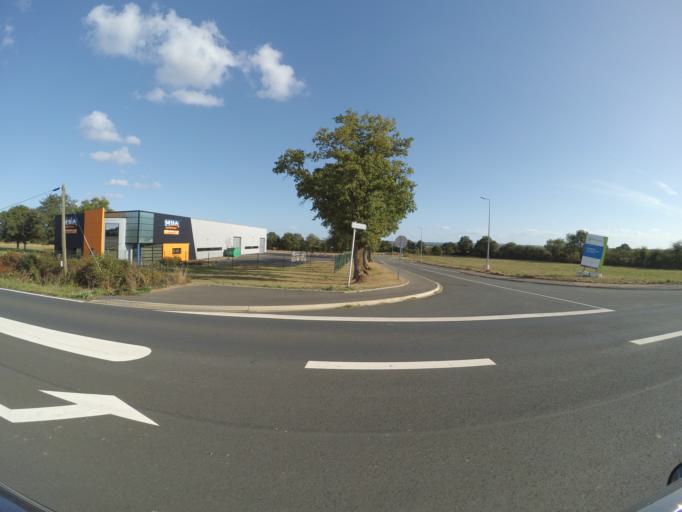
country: FR
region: Pays de la Loire
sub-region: Departement de Maine-et-Loire
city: Torfou
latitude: 47.0358
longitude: -1.0860
